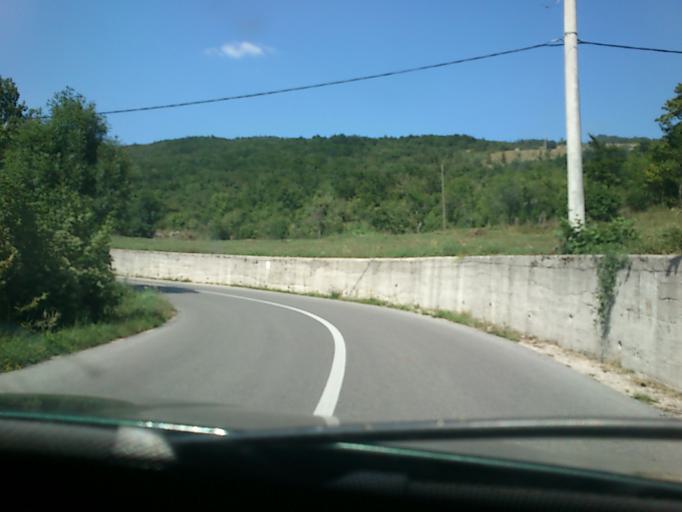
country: HR
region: Licko-Senjska
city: Otocac
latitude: 44.8202
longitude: 15.0801
